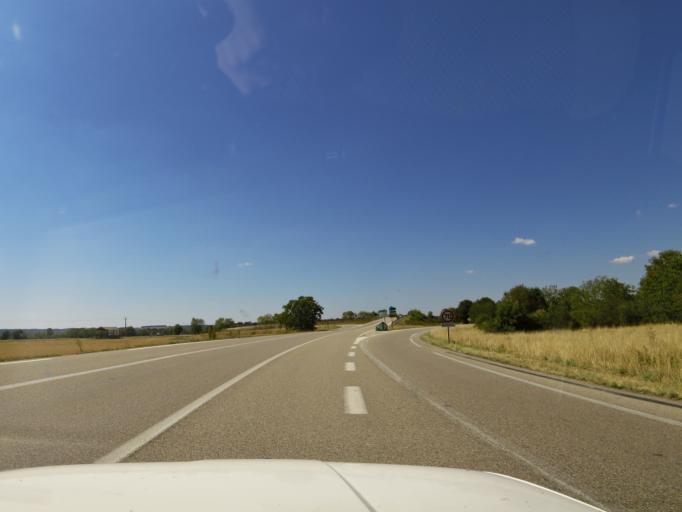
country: FR
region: Rhone-Alpes
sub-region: Departement de l'Ain
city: Saint-Denis-en-Bugey
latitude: 45.9454
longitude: 5.3209
